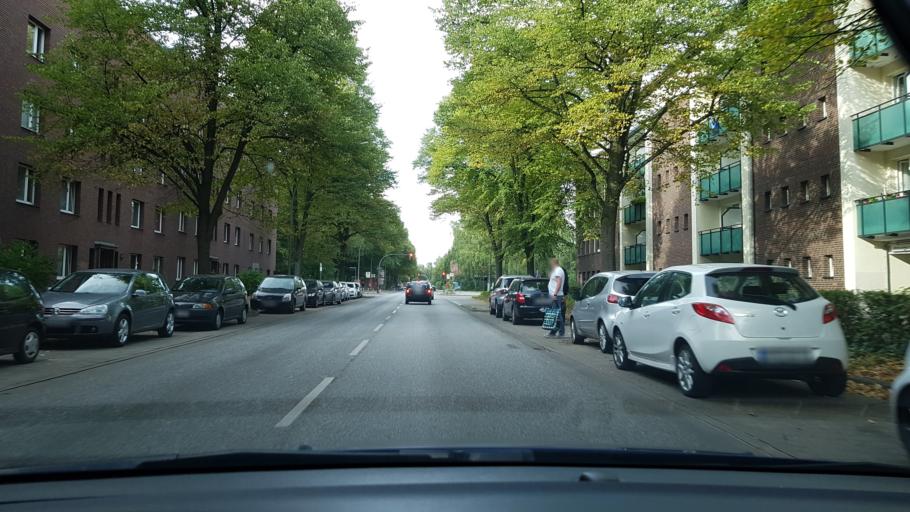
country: DE
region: Hamburg
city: Barmbek-Nord
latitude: 53.5984
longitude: 10.0507
